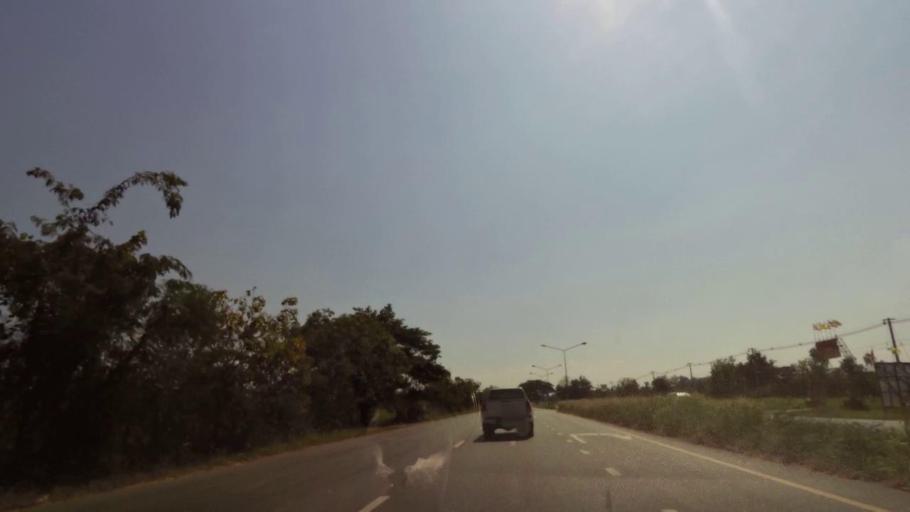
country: TH
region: Nakhon Sawan
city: Kao Liao
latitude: 15.8641
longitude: 100.1167
